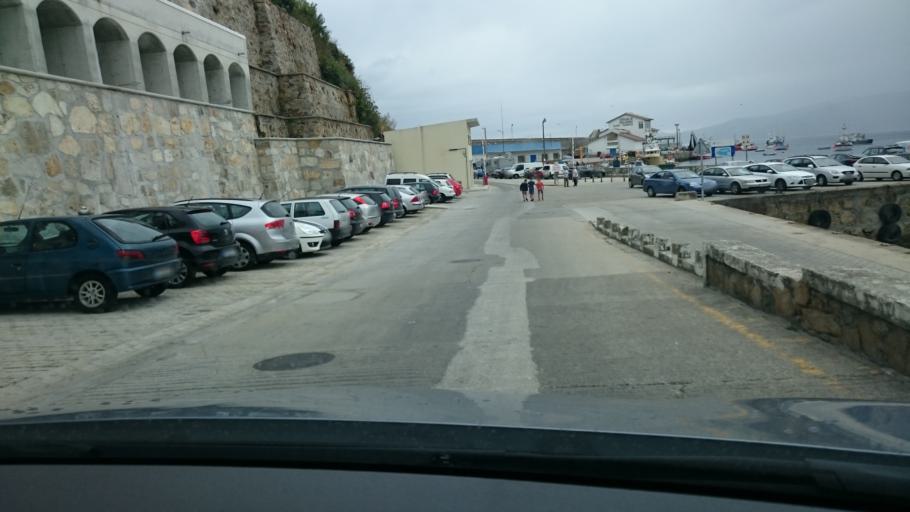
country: ES
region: Galicia
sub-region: Provincia da Coruna
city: Malpica
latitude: 43.3238
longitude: -8.8089
